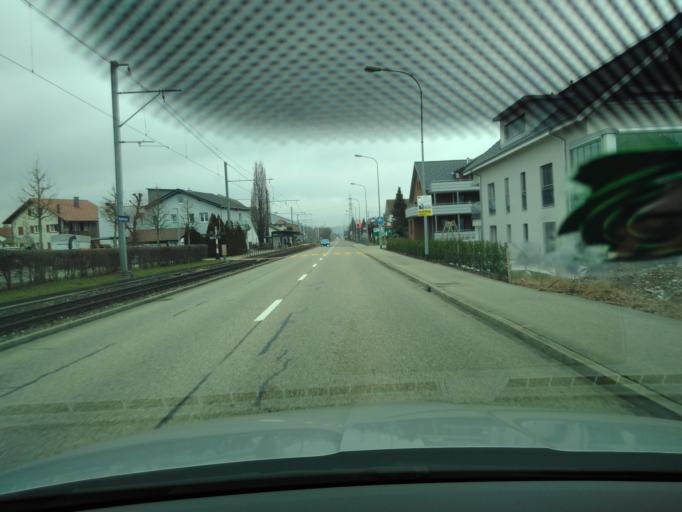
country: CH
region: Aargau
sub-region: Bezirk Aarau
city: Muhen
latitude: 47.3426
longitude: 8.0534
